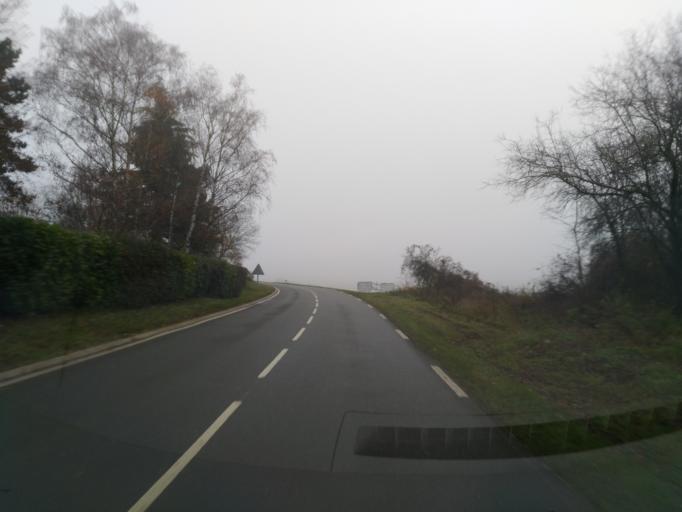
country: FR
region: Ile-de-France
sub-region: Departement des Yvelines
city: Chavenay
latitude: 48.8536
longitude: 1.9947
